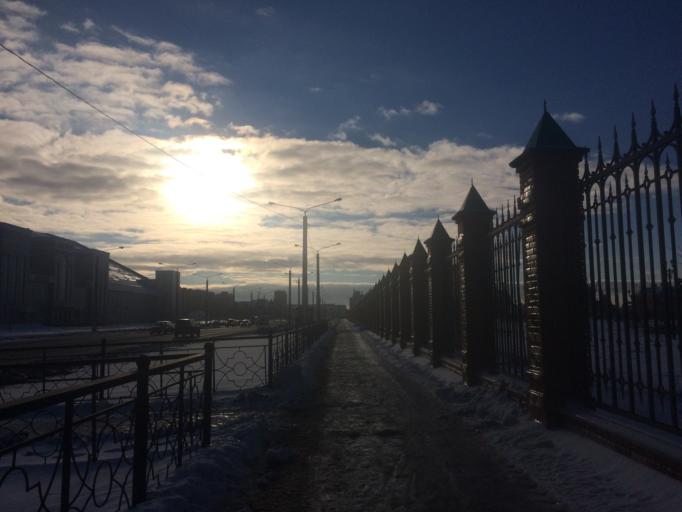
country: RU
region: Mariy-El
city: Yoshkar-Ola
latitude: 56.6411
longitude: 47.9153
